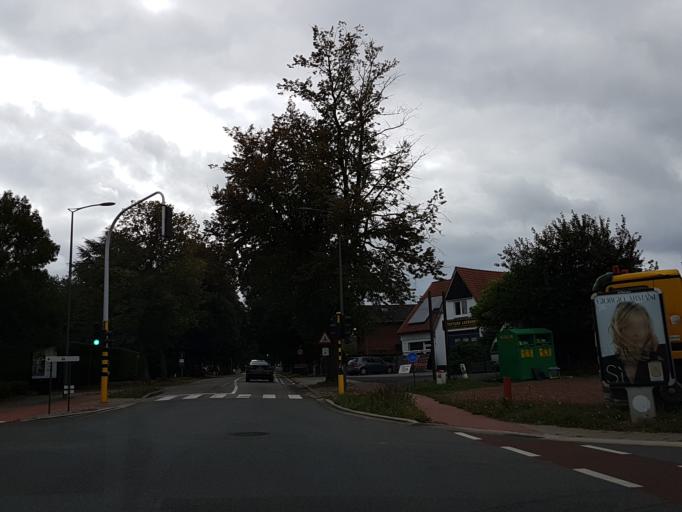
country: BE
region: Flanders
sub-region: Provincie Vlaams-Brabant
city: Wezembeek-Oppem
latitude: 50.8500
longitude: 4.5054
